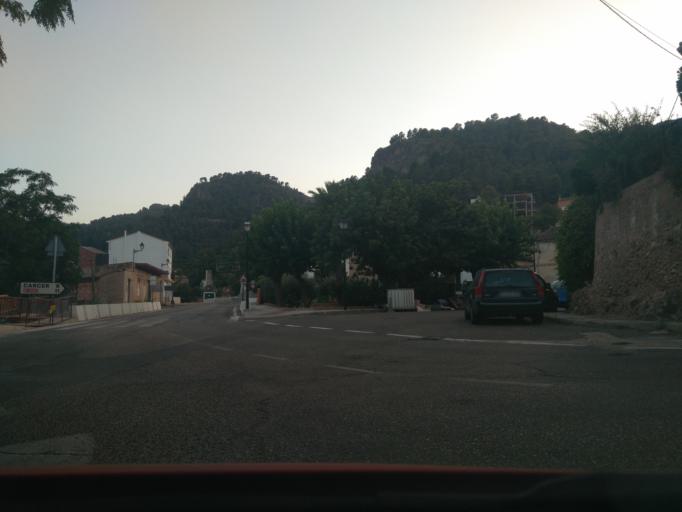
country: ES
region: Valencia
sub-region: Provincia de Valencia
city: Sumacarcer
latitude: 39.0920
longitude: -0.6284
